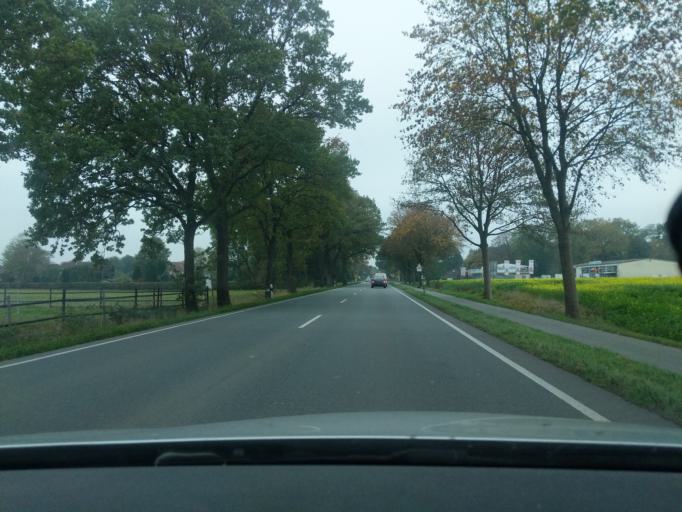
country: DE
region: Lower Saxony
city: Dudenbuttel
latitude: 53.5926
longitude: 9.3614
